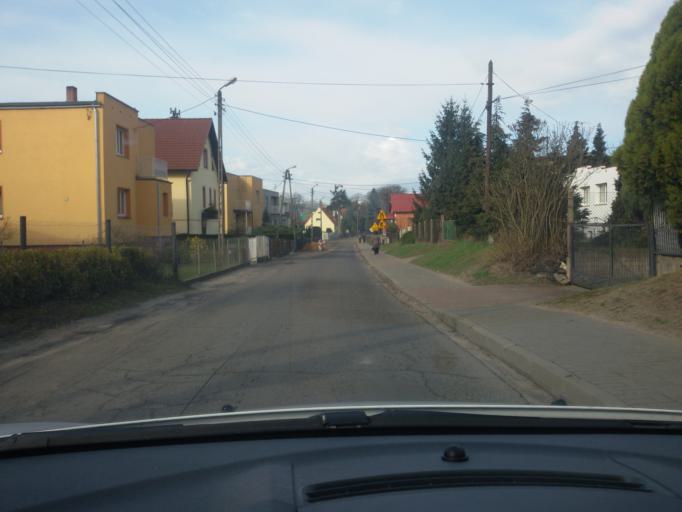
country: PL
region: Lubusz
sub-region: Powiat nowosolski
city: Bytom Odrzanski
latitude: 51.7298
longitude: 15.8213
